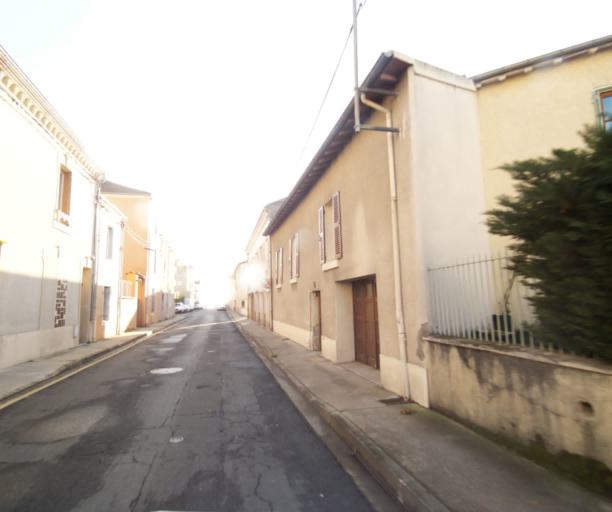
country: FR
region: Rhone-Alpes
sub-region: Departement de la Loire
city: Roanne
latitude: 46.0440
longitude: 4.0656
